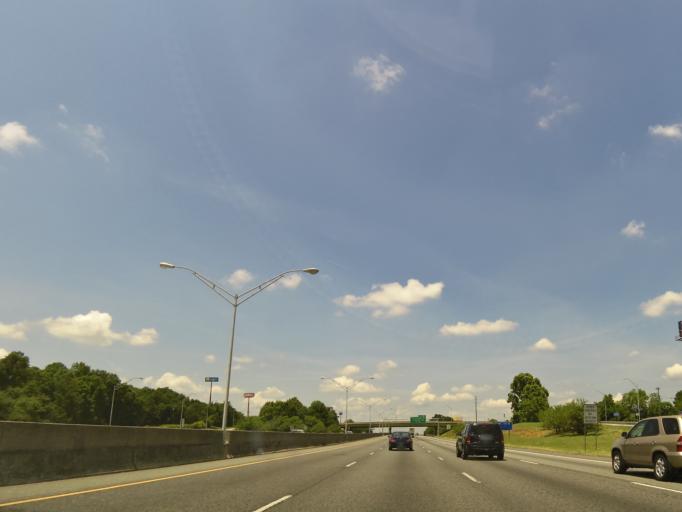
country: US
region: Georgia
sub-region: Monroe County
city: Forsyth
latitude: 33.0264
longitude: -83.9066
